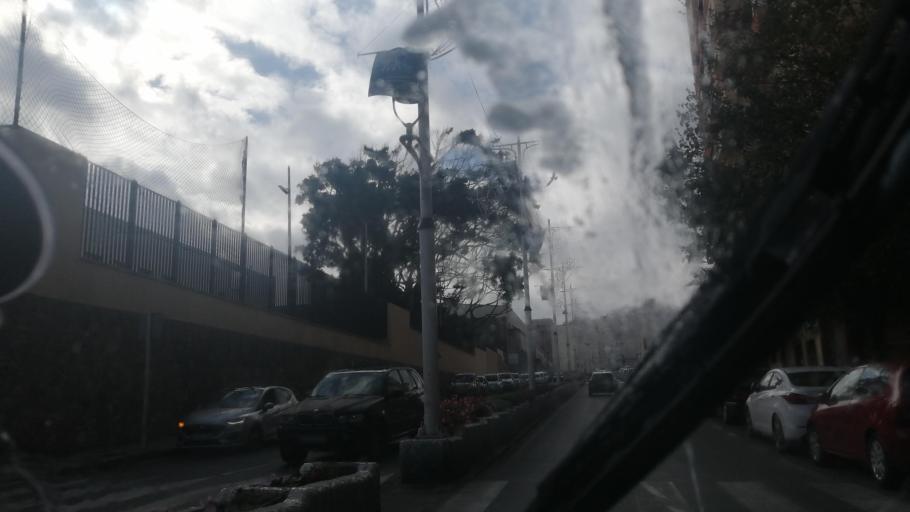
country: ES
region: Ceuta
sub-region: Ceuta
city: Ceuta
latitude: 35.8882
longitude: -5.3223
